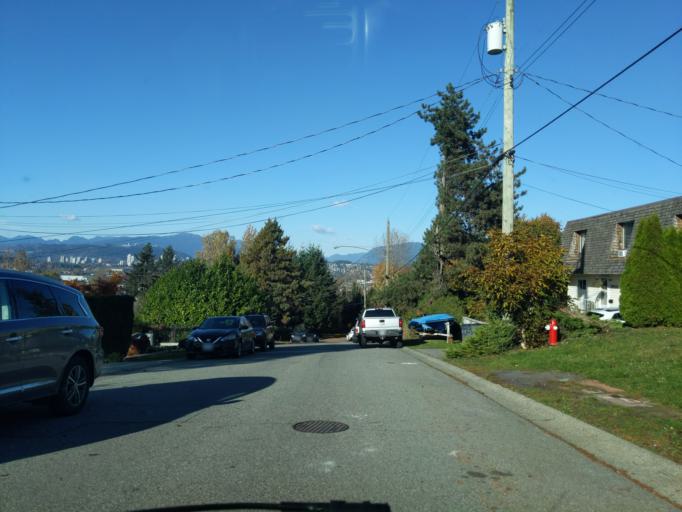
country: CA
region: British Columbia
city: New Westminster
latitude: 49.2017
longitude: -122.8661
